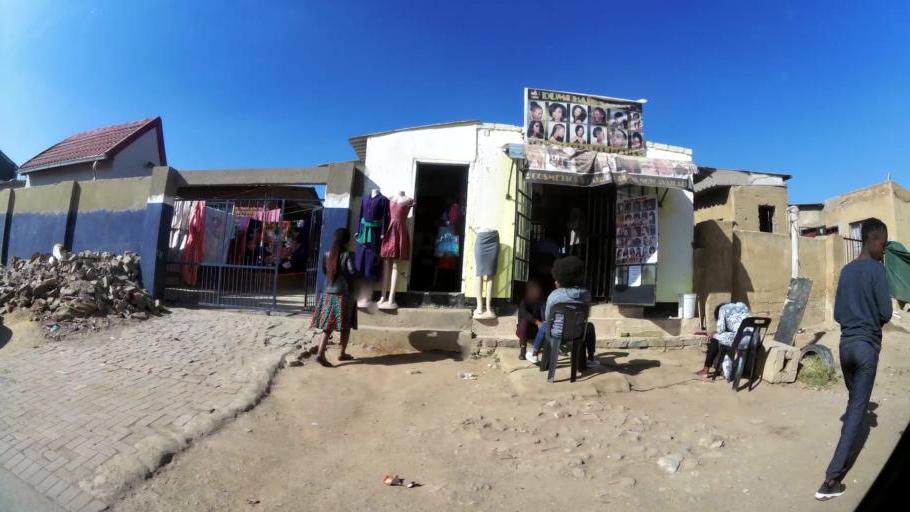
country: ZA
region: Gauteng
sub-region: West Rand District Municipality
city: Muldersdriseloop
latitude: -26.0236
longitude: 27.9204
